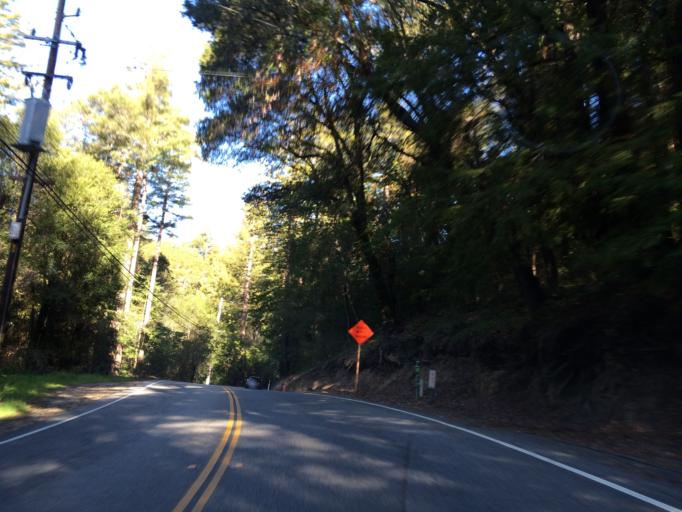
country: US
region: California
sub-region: Santa Cruz County
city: Boulder Creek
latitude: 37.1903
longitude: -122.1440
